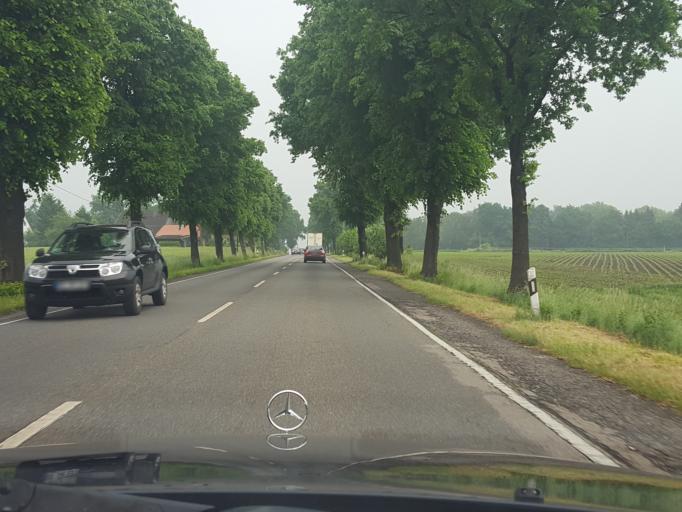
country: DE
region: North Rhine-Westphalia
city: Oer-Erkenschwick
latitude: 51.6304
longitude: 7.2389
